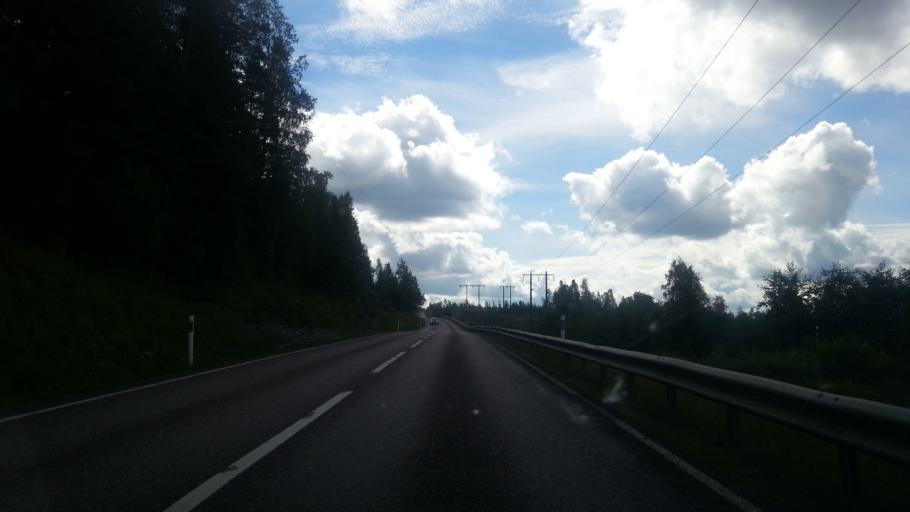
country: SE
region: Dalarna
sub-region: Ludvika Kommun
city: Grangesberg
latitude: 60.0356
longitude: 14.9692
